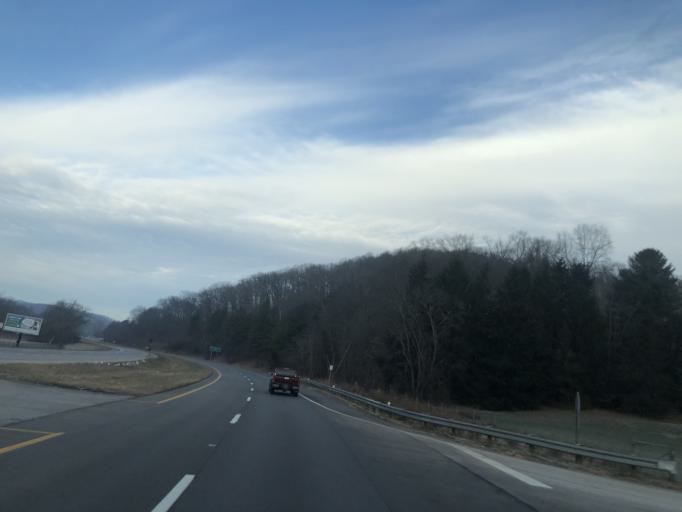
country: US
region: Ohio
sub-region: Athens County
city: Chauncey
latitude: 39.4047
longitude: -82.1713
